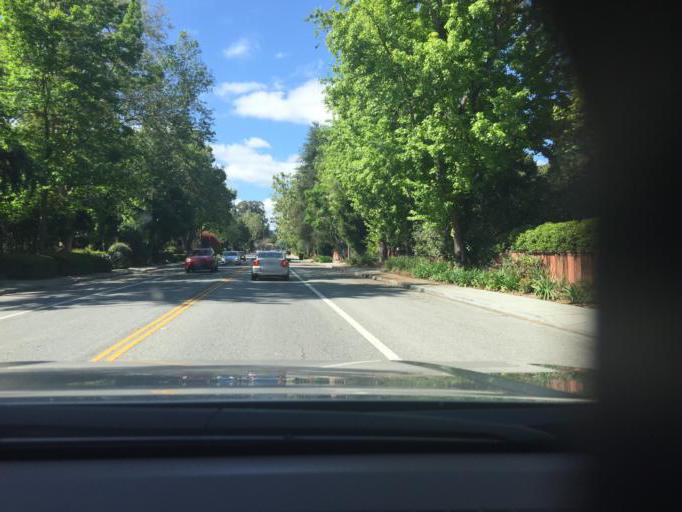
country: US
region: California
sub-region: San Mateo County
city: Menlo Park
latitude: 37.4580
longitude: -122.1623
